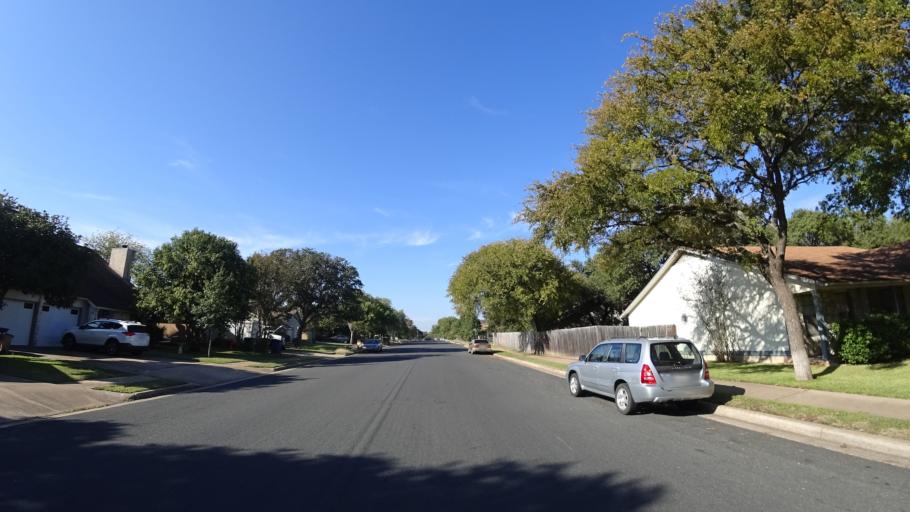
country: US
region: Texas
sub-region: Travis County
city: Shady Hollow
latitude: 30.2102
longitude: -97.8492
